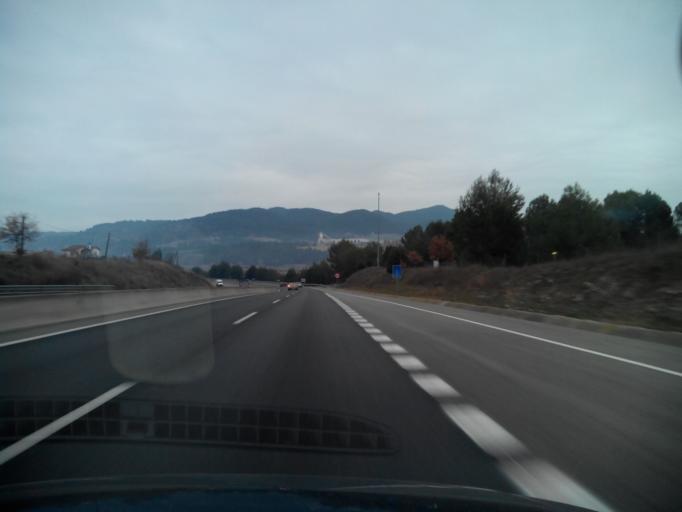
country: ES
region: Catalonia
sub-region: Provincia de Barcelona
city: Sallent
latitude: 41.7925
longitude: 1.8972
